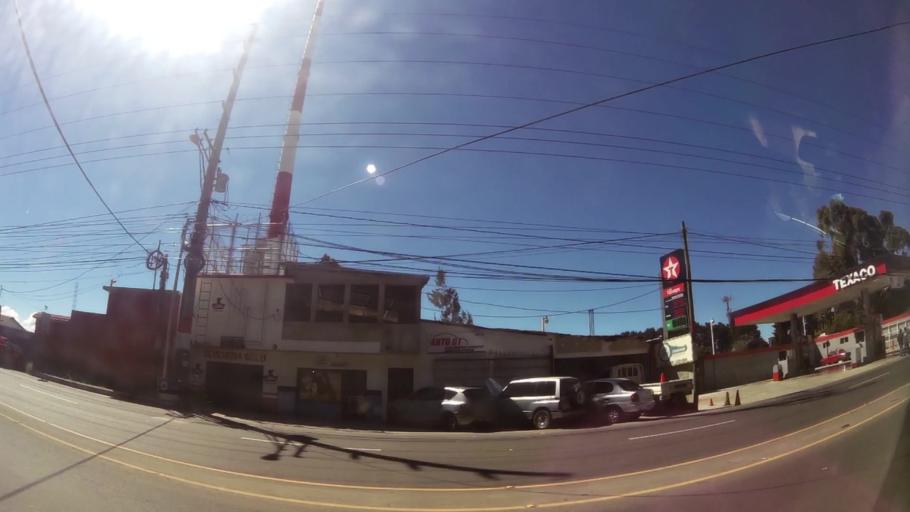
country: GT
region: Guatemala
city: San Jose Pinula
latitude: 14.5442
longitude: -90.4424
